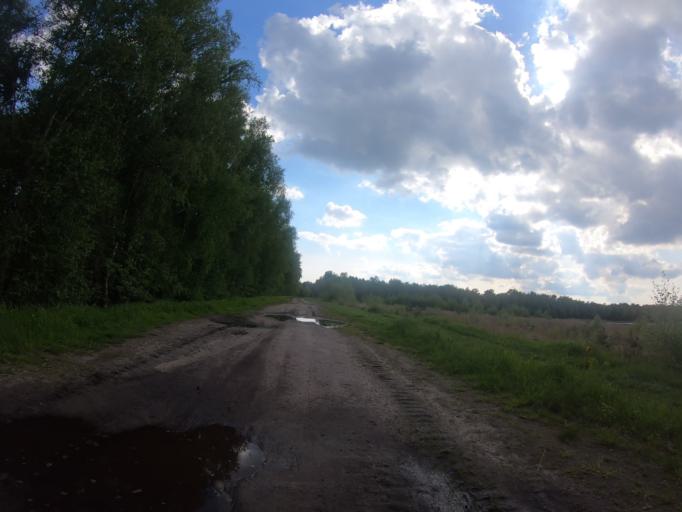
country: DE
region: Lower Saxony
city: Sassenburg
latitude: 52.5147
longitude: 10.6197
